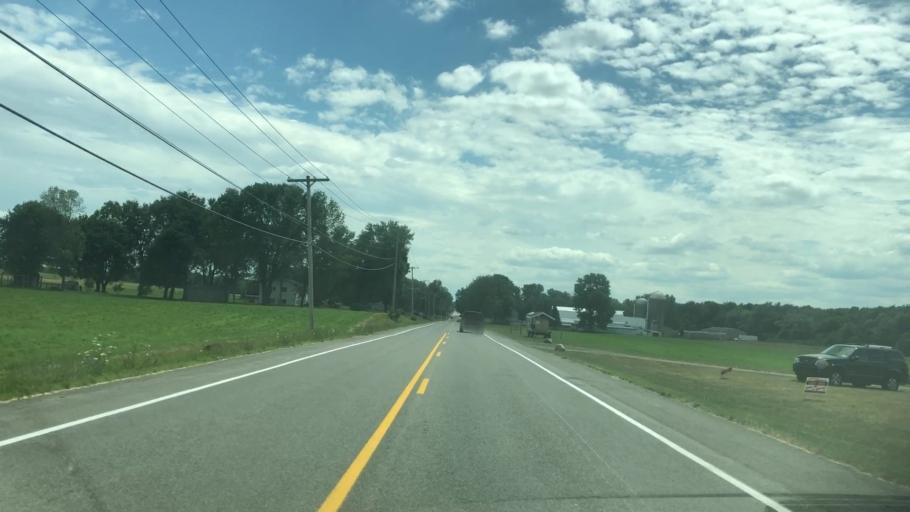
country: US
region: New York
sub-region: Monroe County
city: Fairport
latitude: 43.1514
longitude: -77.4006
